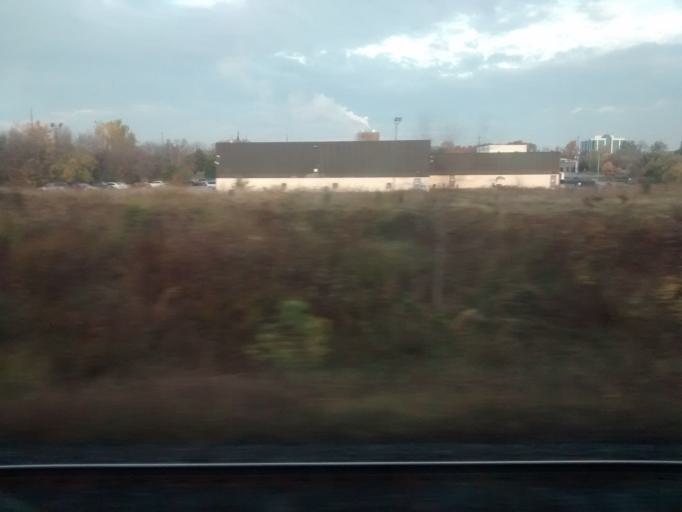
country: CA
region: Ontario
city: Burlington
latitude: 43.3842
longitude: -79.7563
